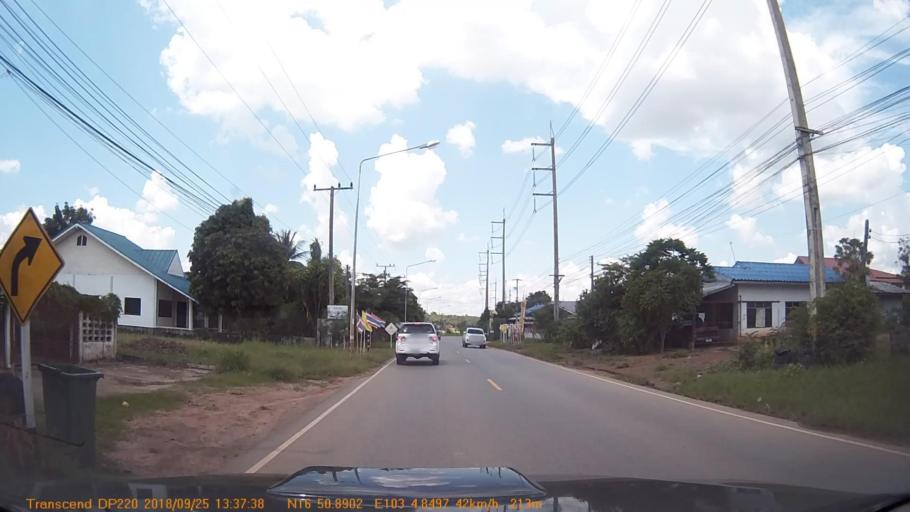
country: TH
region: Khon Kaen
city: Kranuan
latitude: 16.8481
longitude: 103.0808
